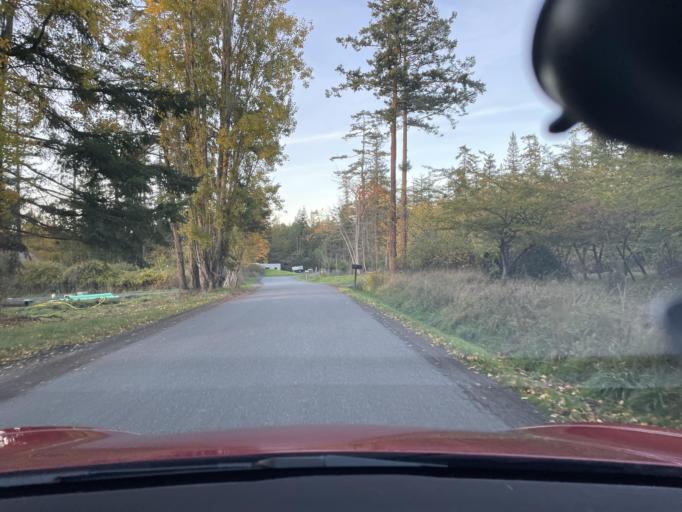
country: US
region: Washington
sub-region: San Juan County
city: Friday Harbor
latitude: 48.6172
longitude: -123.1510
